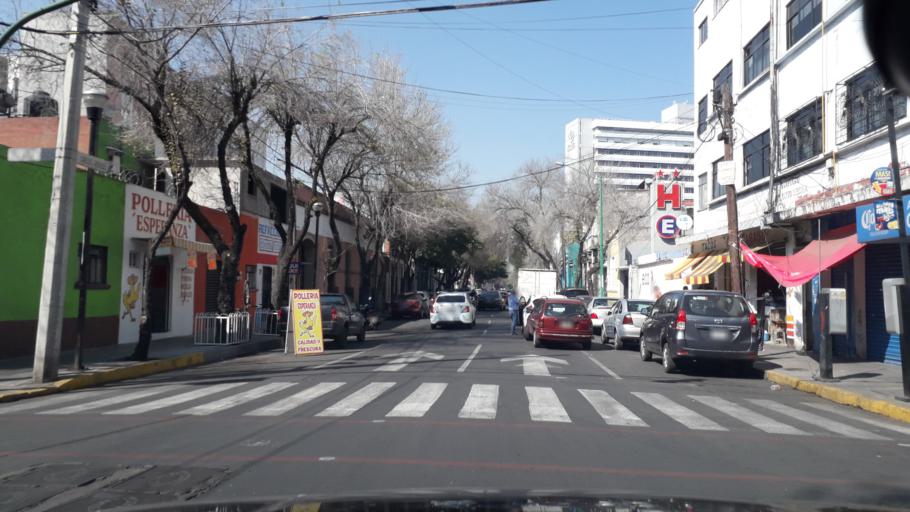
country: MX
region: Mexico City
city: Cuauhtemoc
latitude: 19.4436
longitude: -99.1493
